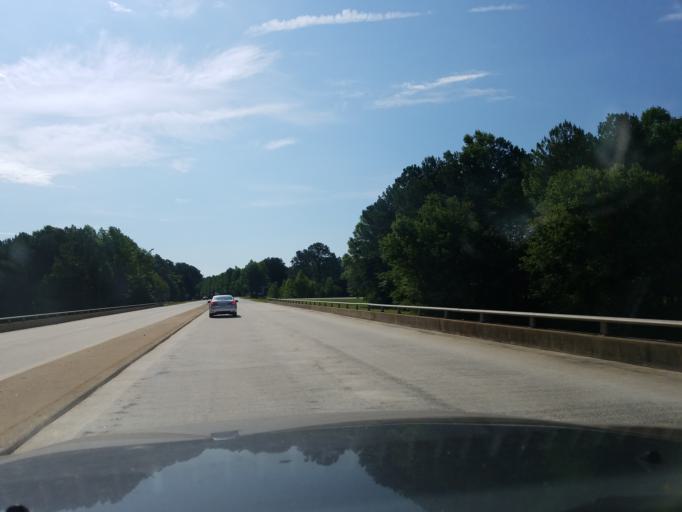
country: US
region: North Carolina
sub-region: Granville County
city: Oxford
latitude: 36.3149
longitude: -78.5441
